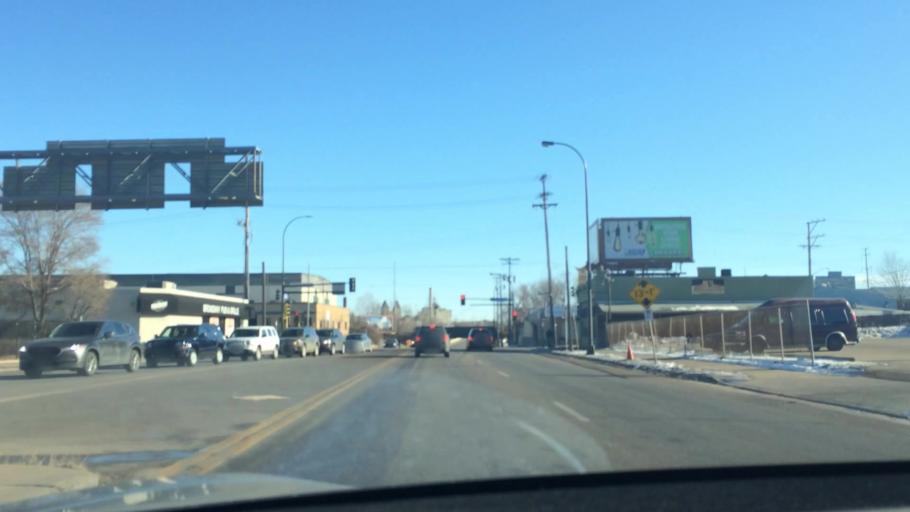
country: US
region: Minnesota
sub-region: Hennepin County
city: Minneapolis
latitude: 44.9991
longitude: -93.2814
